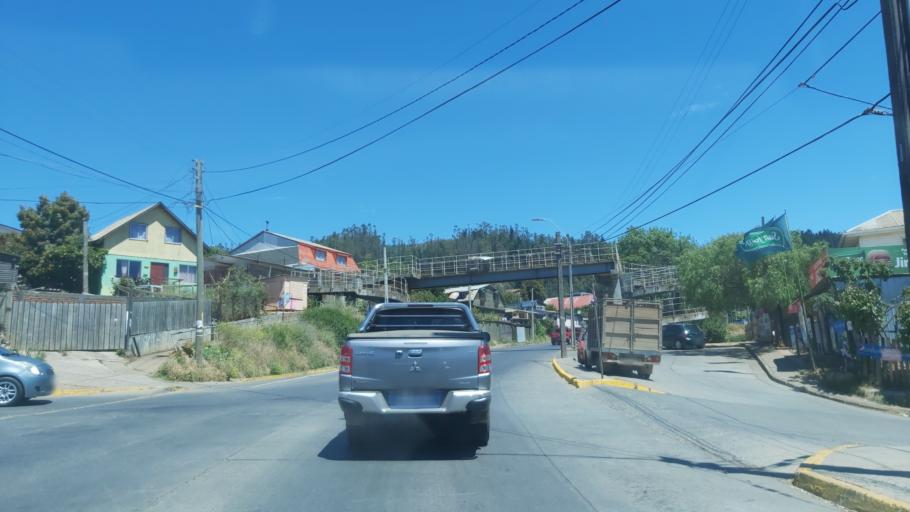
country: CL
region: Maule
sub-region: Provincia de Talca
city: Constitucion
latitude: -35.3424
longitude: -72.4171
